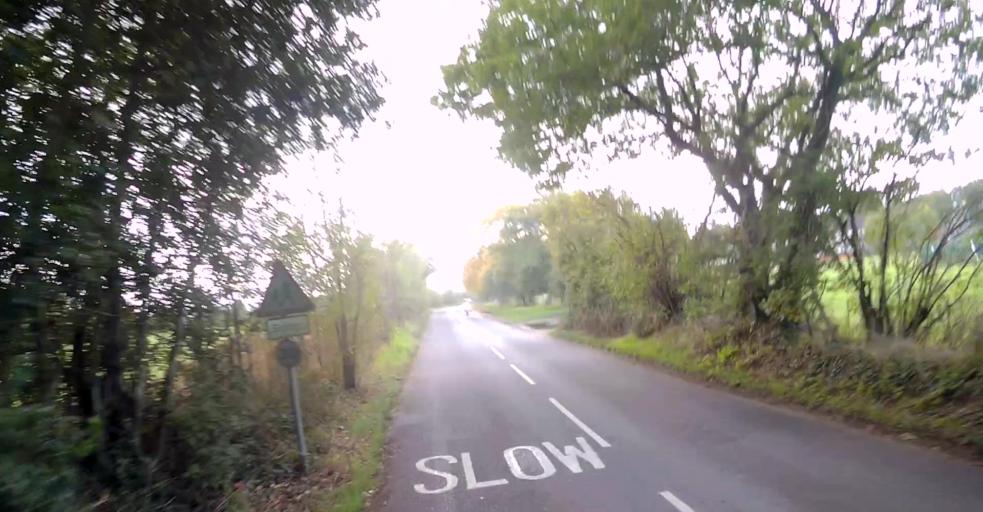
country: GB
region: England
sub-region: Surrey
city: Seale
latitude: 51.1921
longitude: -0.7467
